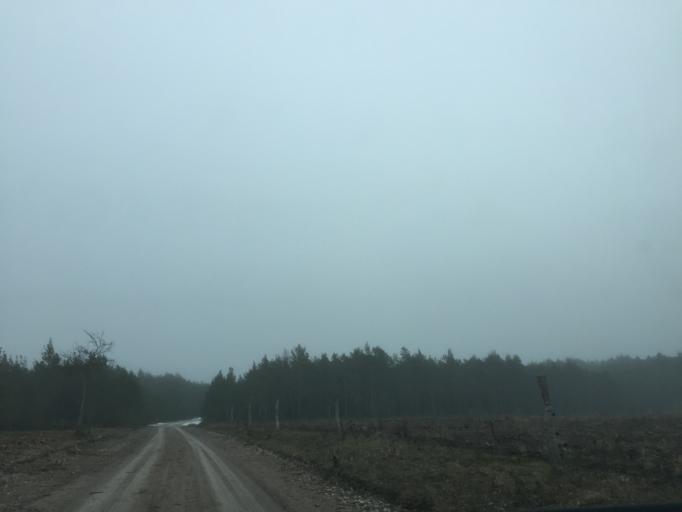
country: EE
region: Saare
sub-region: Kuressaare linn
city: Kuressaare
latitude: 58.5078
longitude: 21.9565
